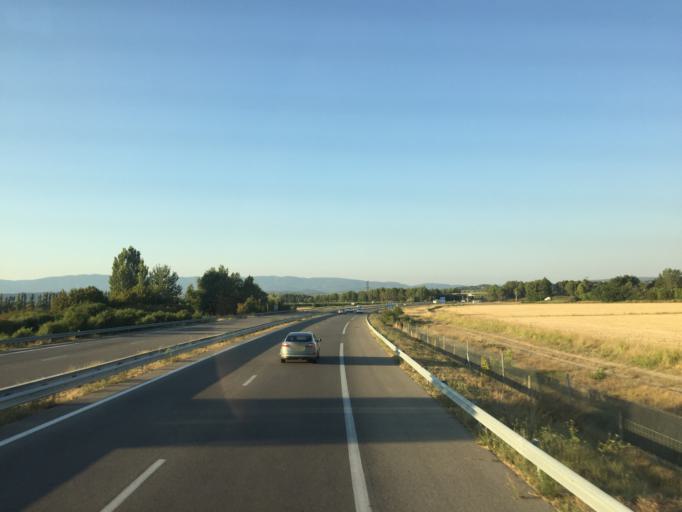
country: FR
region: Provence-Alpes-Cote d'Azur
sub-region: Departement des Bouches-du-Rhone
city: Meyrargues
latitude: 43.6534
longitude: 5.4937
